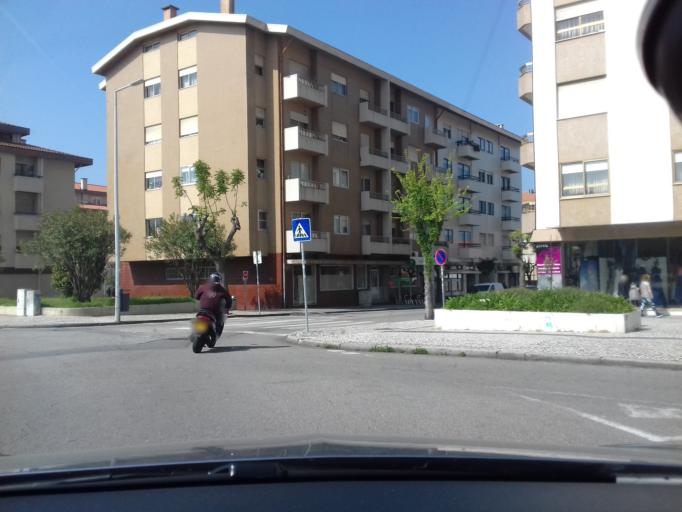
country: PT
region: Aveiro
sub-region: Espinho
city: Espinho
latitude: 41.0041
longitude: -8.6344
